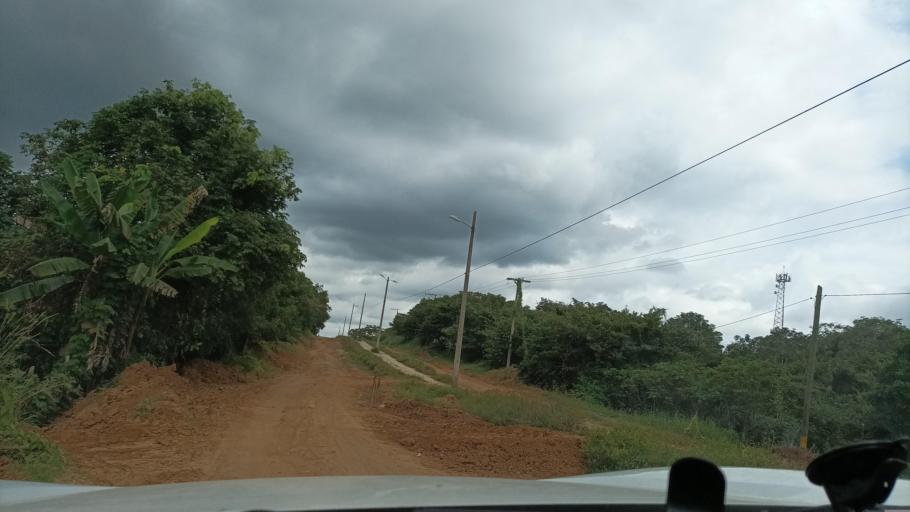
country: MX
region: Veracruz
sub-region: Soconusco
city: Fraccionamiento Santa Cruz
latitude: 17.9646
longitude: -94.8934
